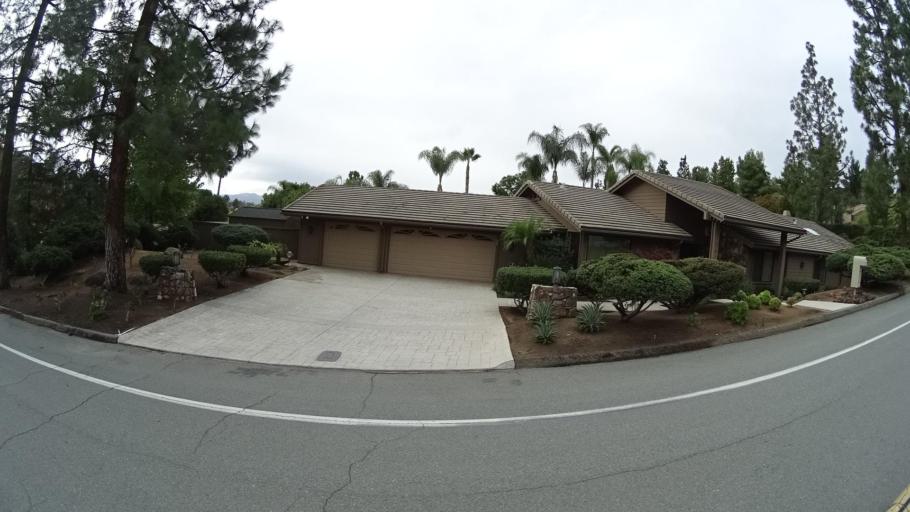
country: US
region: California
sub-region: San Diego County
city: Granite Hills
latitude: 32.7742
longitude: -116.9124
